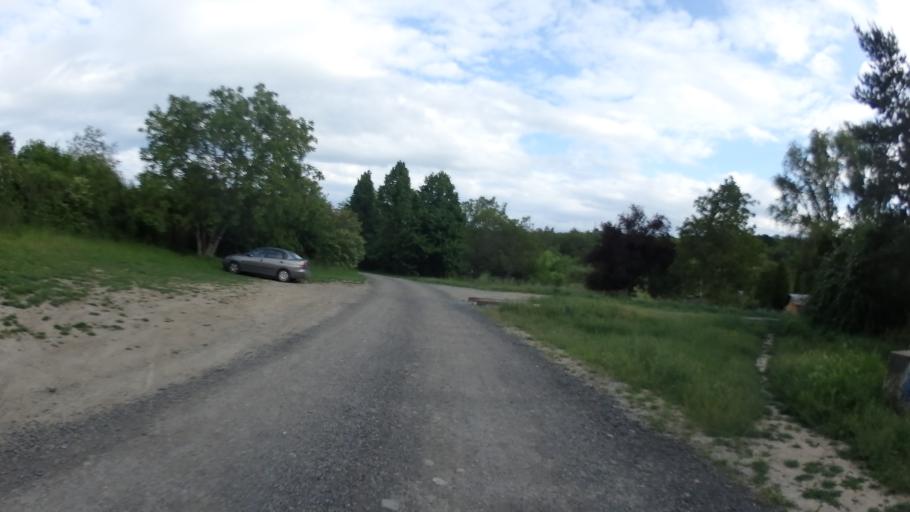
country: CZ
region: South Moravian
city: Moravany
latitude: 49.1637
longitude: 16.5872
